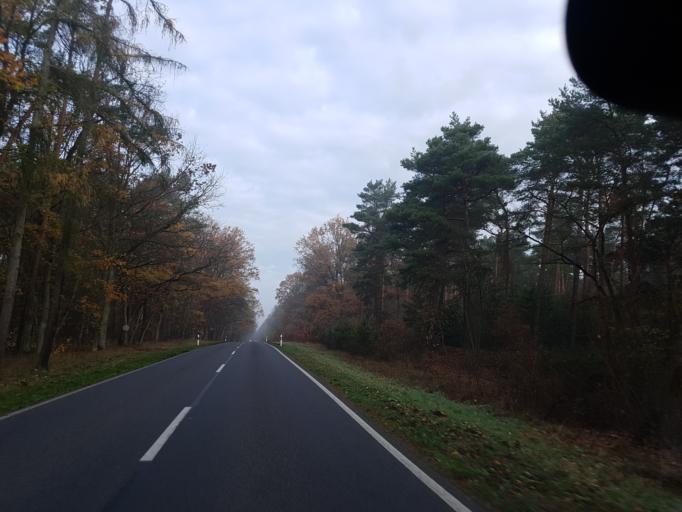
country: DE
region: Saxony-Anhalt
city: Kropstadt
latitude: 51.9426
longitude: 12.7551
